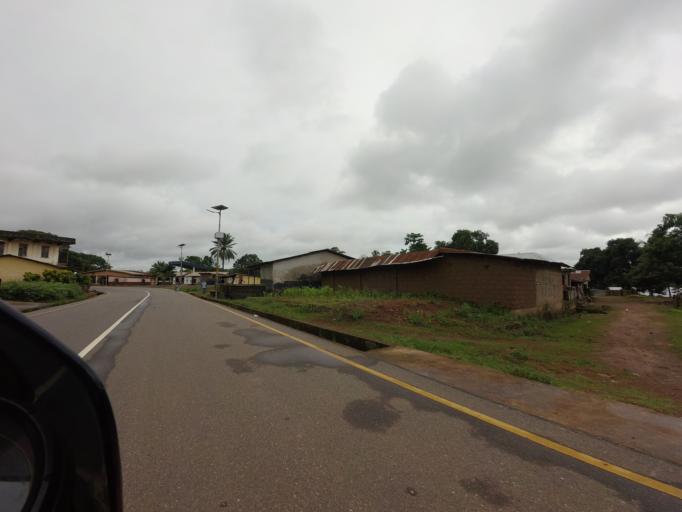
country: SL
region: Northern Province
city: Kambia
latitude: 9.1279
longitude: -12.9212
